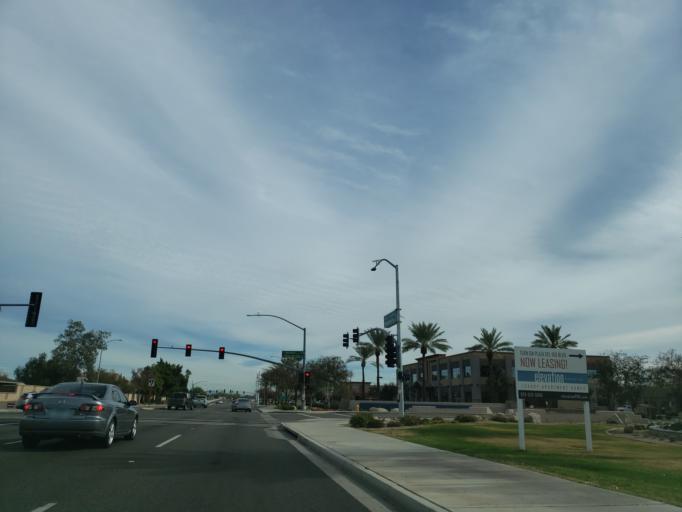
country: US
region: Arizona
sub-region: Maricopa County
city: Sun City
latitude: 33.6096
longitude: -112.2581
